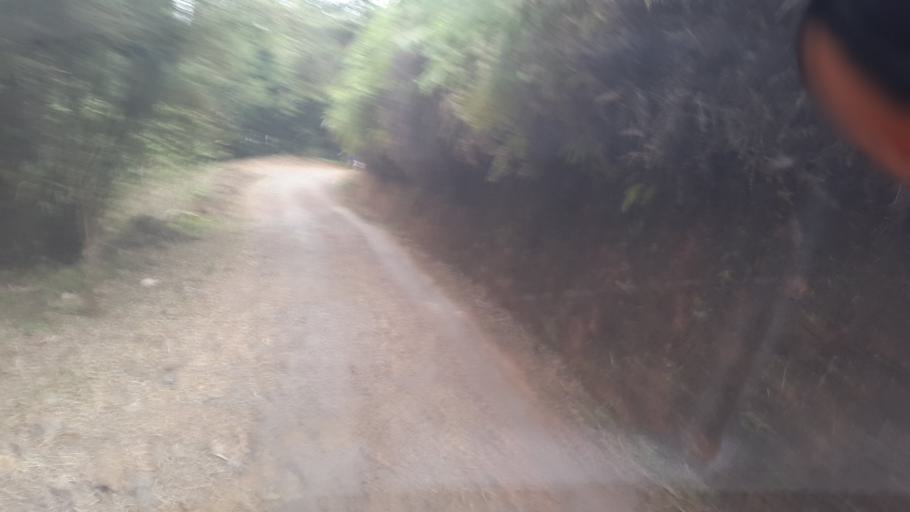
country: ID
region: West Java
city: Cigawir
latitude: -7.0754
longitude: 106.9027
